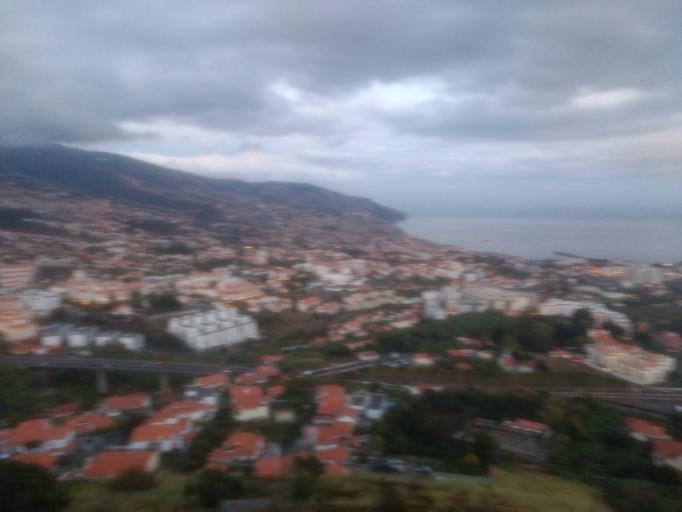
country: PT
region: Madeira
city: Camara de Lobos
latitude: 32.6584
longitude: -16.9390
